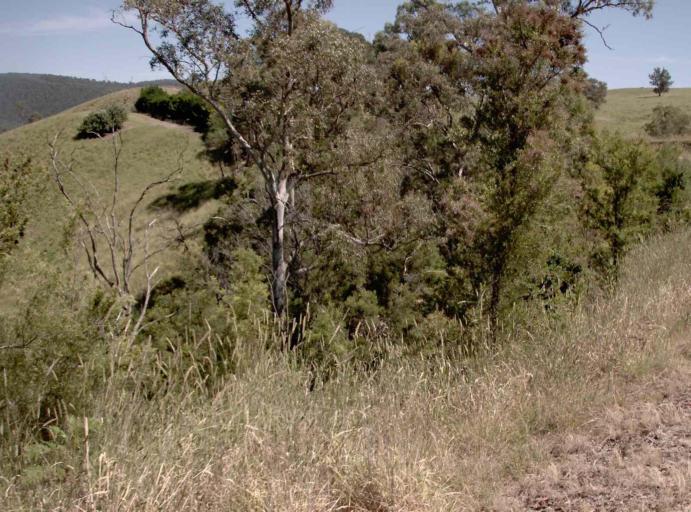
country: AU
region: Victoria
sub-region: East Gippsland
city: Lakes Entrance
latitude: -37.4842
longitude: 148.1869
